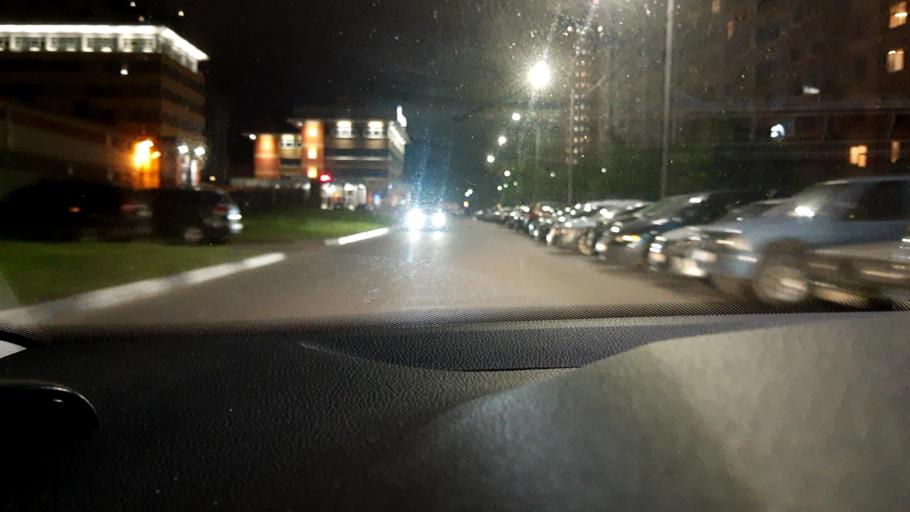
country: RU
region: Moskovskaya
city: Opalikha
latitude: 55.8323
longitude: 37.2920
